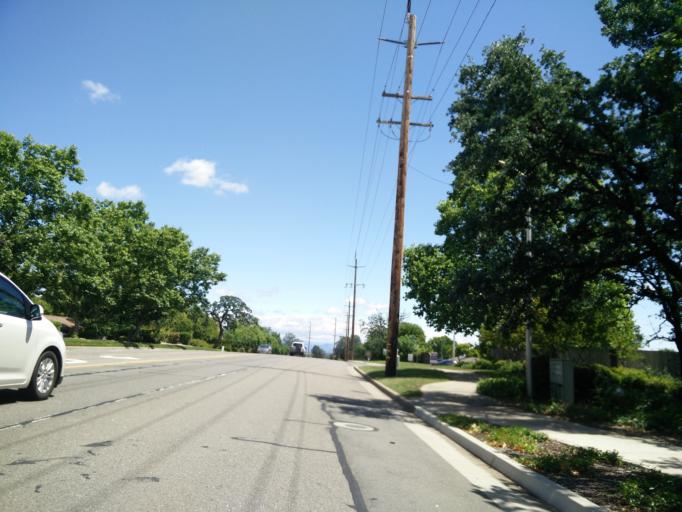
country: US
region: California
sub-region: Shasta County
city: Redding
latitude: 40.5964
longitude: -122.3664
